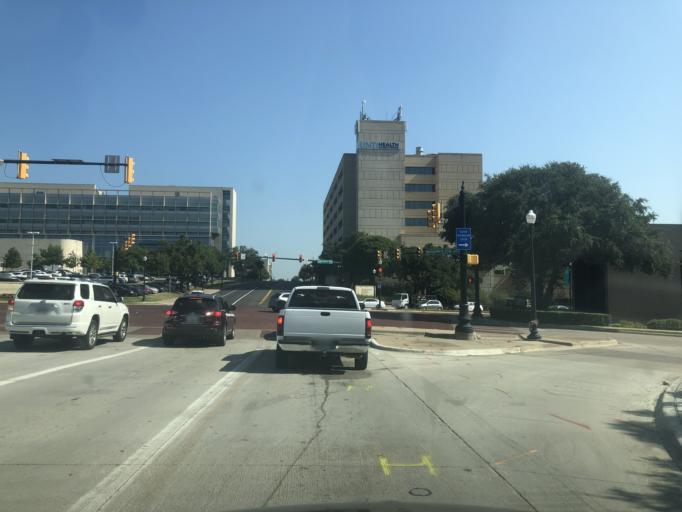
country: US
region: Texas
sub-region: Tarrant County
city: River Oaks
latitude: 32.7472
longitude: -97.3699
